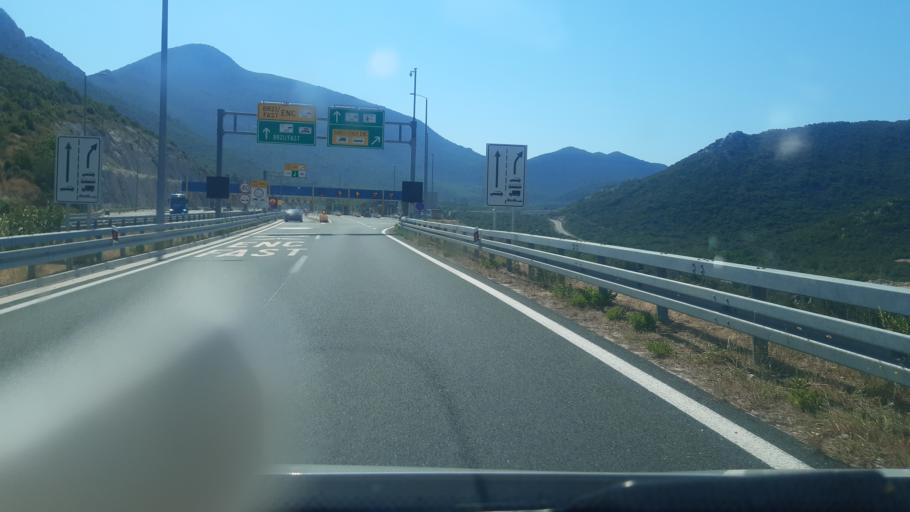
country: HR
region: Dubrovacko-Neretvanska
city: Komin
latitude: 43.1025
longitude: 17.4831
